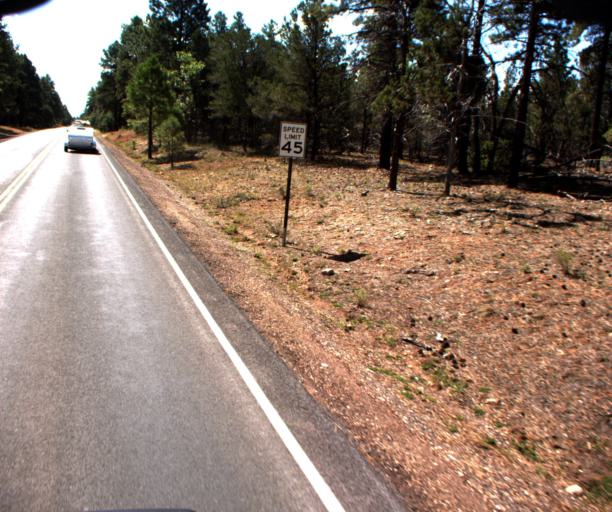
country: US
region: Arizona
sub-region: Coconino County
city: Grand Canyon
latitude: 36.0450
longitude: -112.0835
